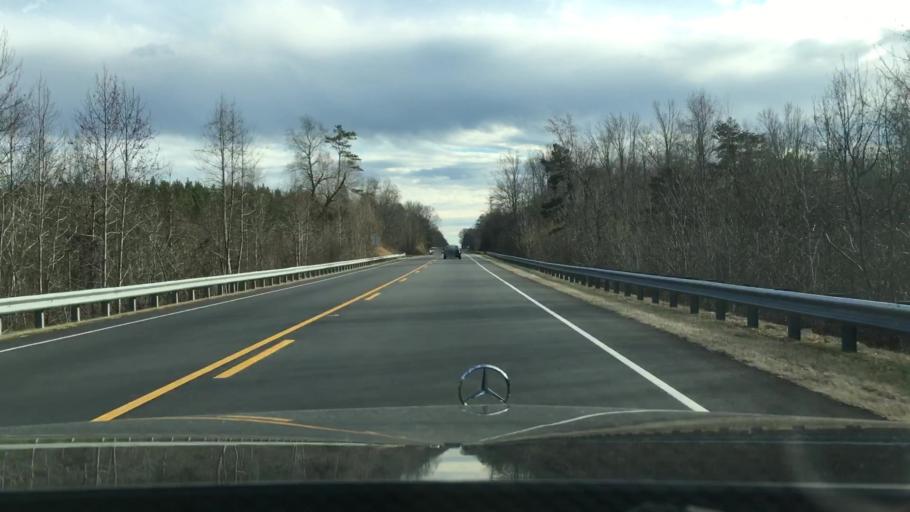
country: US
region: Virginia
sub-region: City of Danville
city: Danville
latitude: 36.4991
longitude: -79.3869
